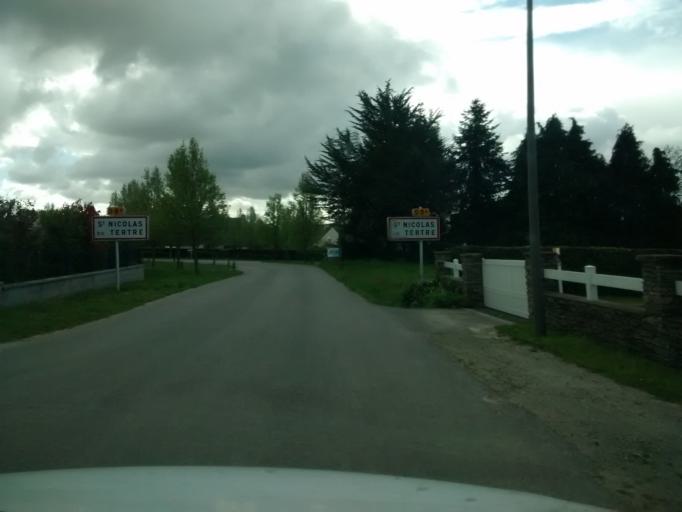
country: FR
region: Brittany
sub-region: Departement du Morbihan
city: Ruffiac
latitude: 47.8023
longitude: -2.2278
